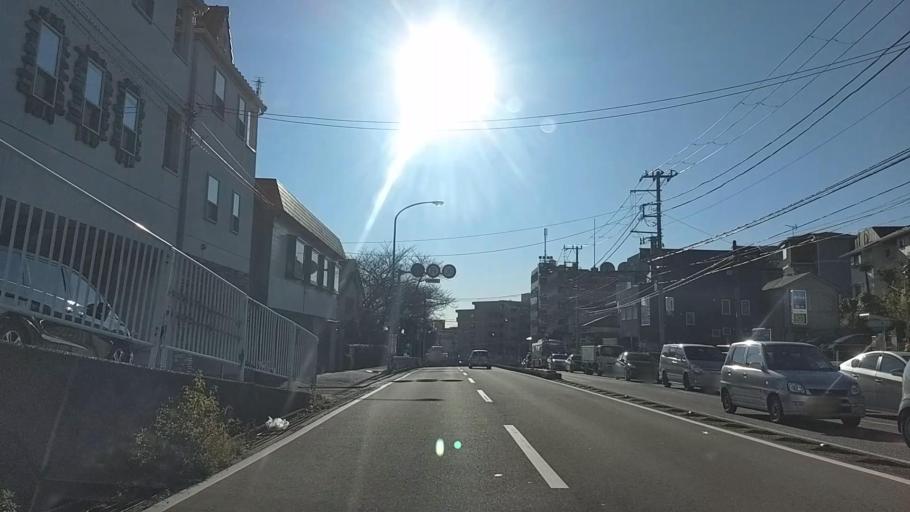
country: JP
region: Kanagawa
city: Yokohama
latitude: 35.4699
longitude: 139.6075
